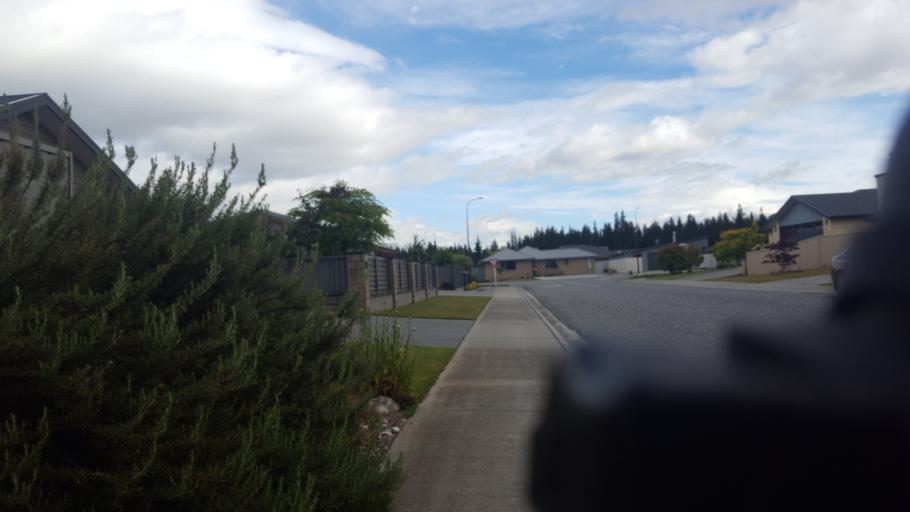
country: NZ
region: Otago
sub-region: Queenstown-Lakes District
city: Wanaka
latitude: -45.2395
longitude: 169.3819
